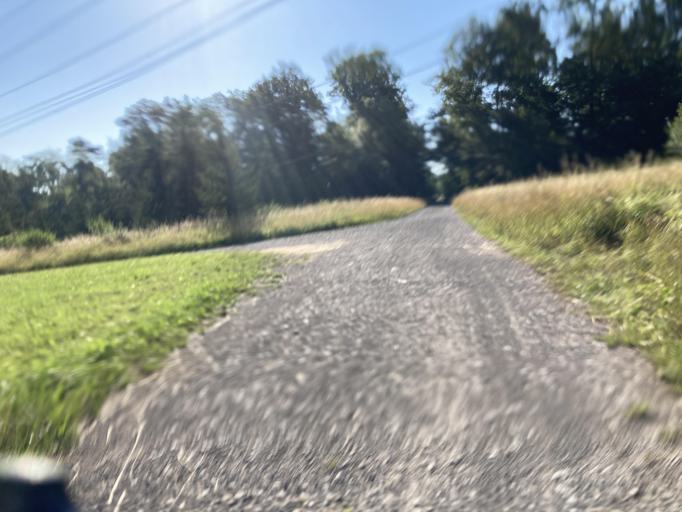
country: DE
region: Baden-Wuerttemberg
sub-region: Regierungsbezirk Stuttgart
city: Renningen
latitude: 48.7828
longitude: 8.9712
